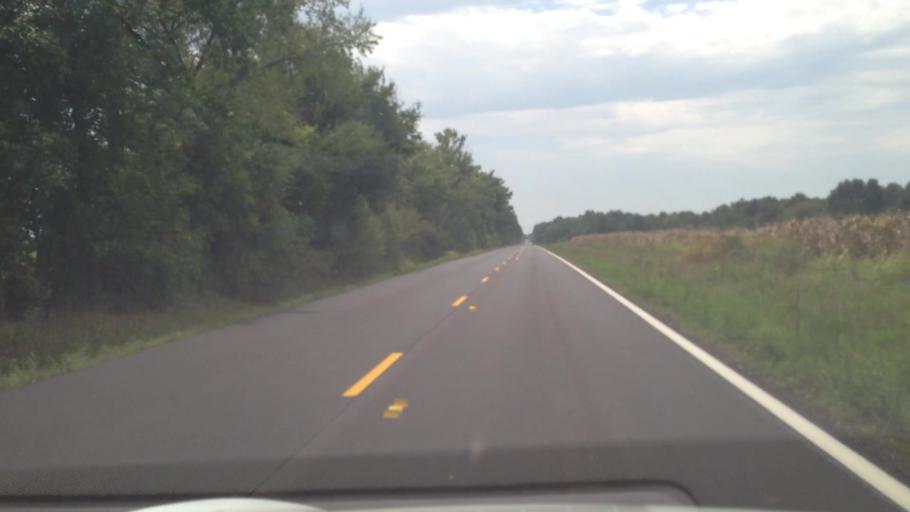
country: US
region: Kansas
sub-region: Crawford County
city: Girard
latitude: 37.5282
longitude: -94.9606
